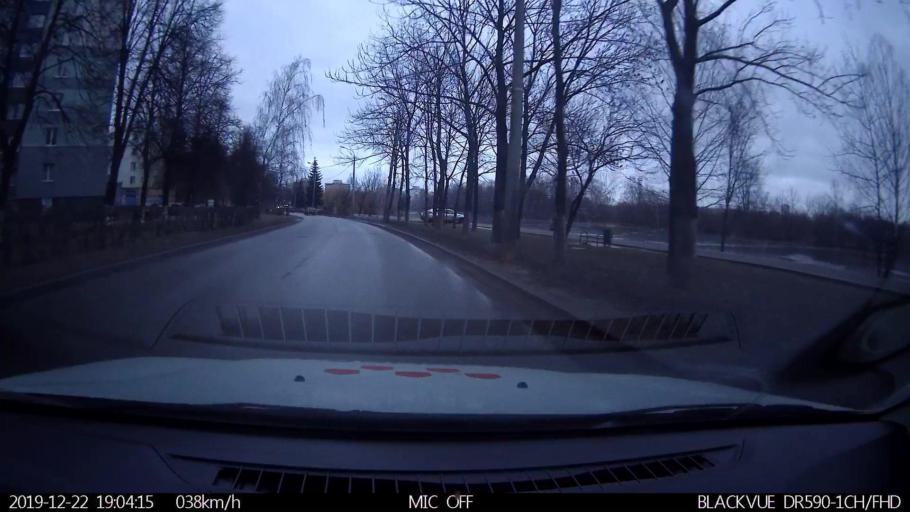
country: RU
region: Nizjnij Novgorod
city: Gorbatovka
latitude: 56.3404
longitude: 43.8478
